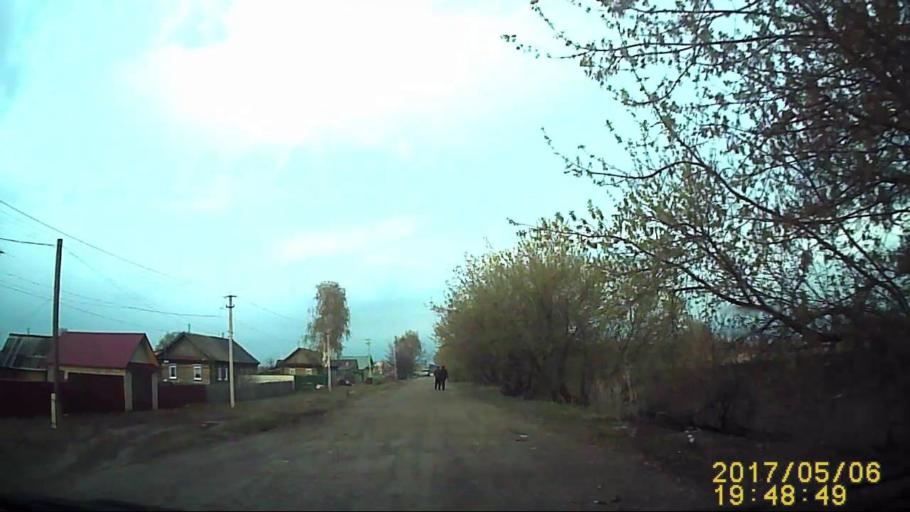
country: RU
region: Ulyanovsk
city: Staraya Mayna
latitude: 54.6009
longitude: 48.9236
